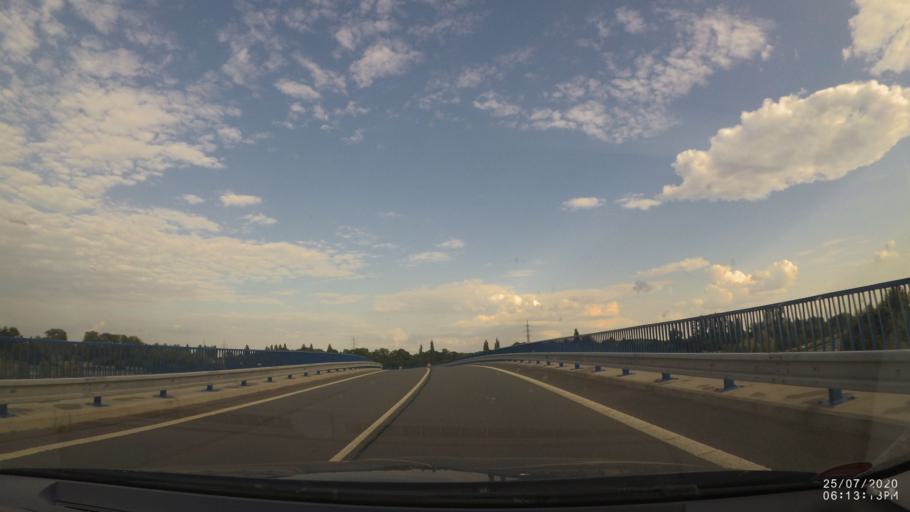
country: CZ
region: Kralovehradecky
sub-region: Okres Hradec Kralove
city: Hradec Kralove
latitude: 50.1861
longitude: 15.8047
